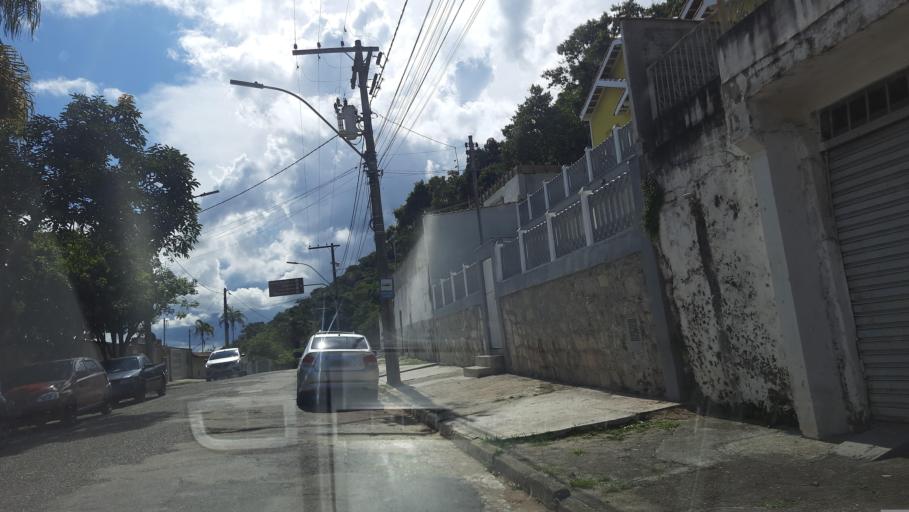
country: BR
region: Minas Gerais
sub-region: Pocos De Caldas
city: Pocos de Caldas
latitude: -21.7781
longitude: -46.5635
